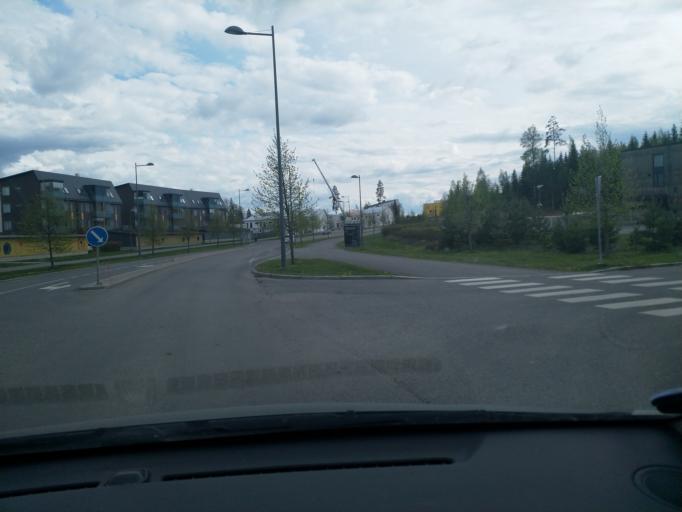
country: FI
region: Pirkanmaa
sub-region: Tampere
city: Tampere
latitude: 61.4380
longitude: 23.8119
